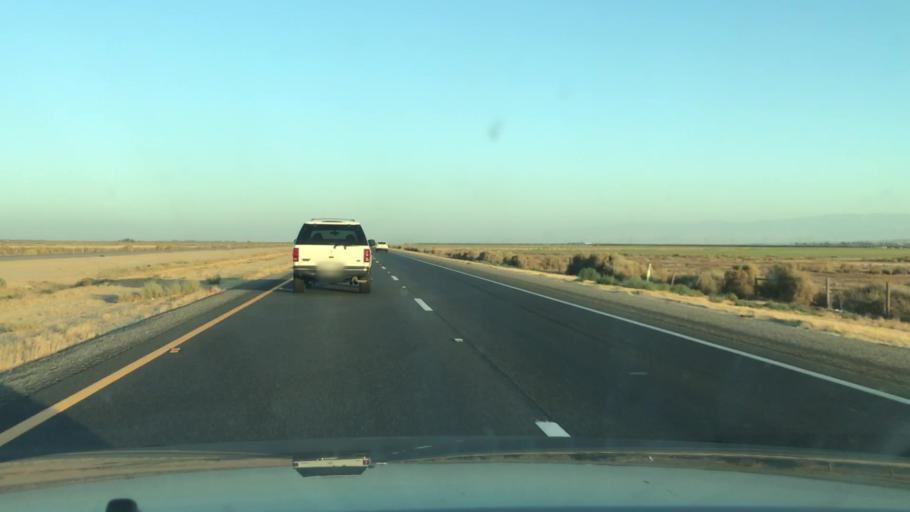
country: US
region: California
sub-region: Kern County
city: Buttonwillow
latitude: 35.3862
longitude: -119.3799
